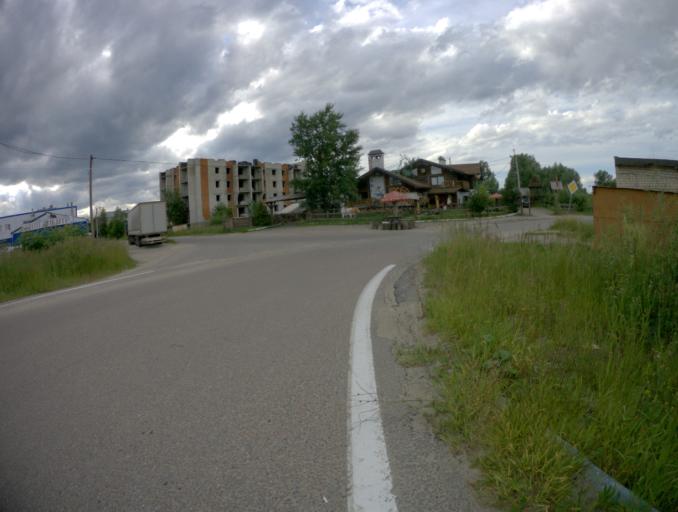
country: RU
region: Vladimir
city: Gorokhovets
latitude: 56.2004
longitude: 42.7086
